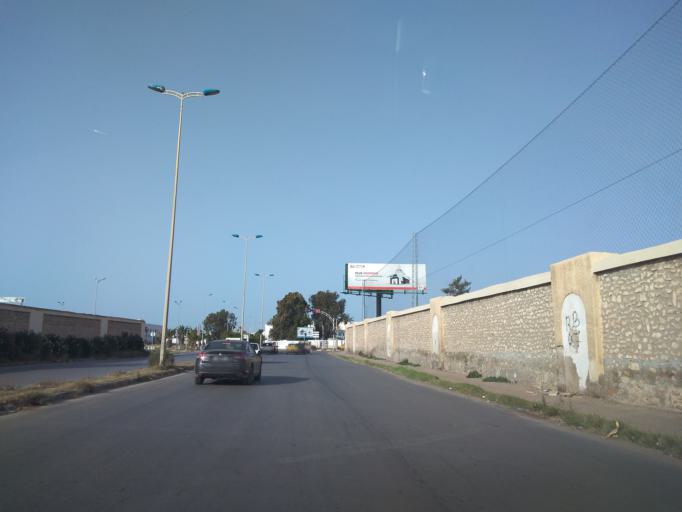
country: TN
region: Safaqis
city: Sfax
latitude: 34.7323
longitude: 10.7468
